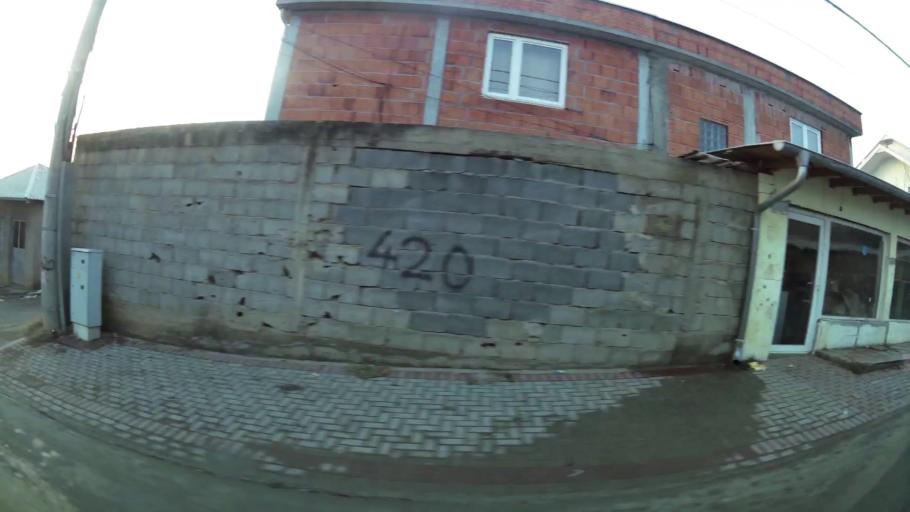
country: MK
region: Aracinovo
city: Arachinovo
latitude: 42.0313
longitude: 21.5657
